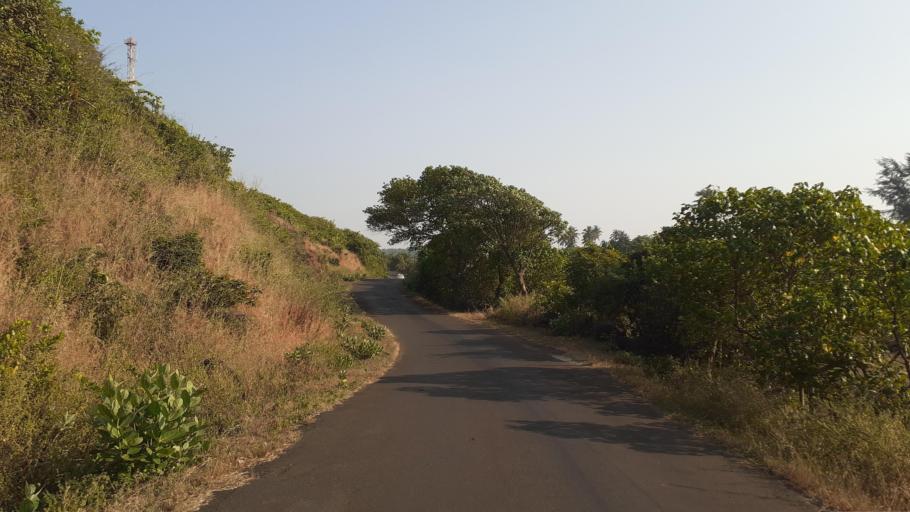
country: IN
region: Maharashtra
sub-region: Ratnagiri
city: Ratnagiri
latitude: 17.2205
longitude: 73.2456
